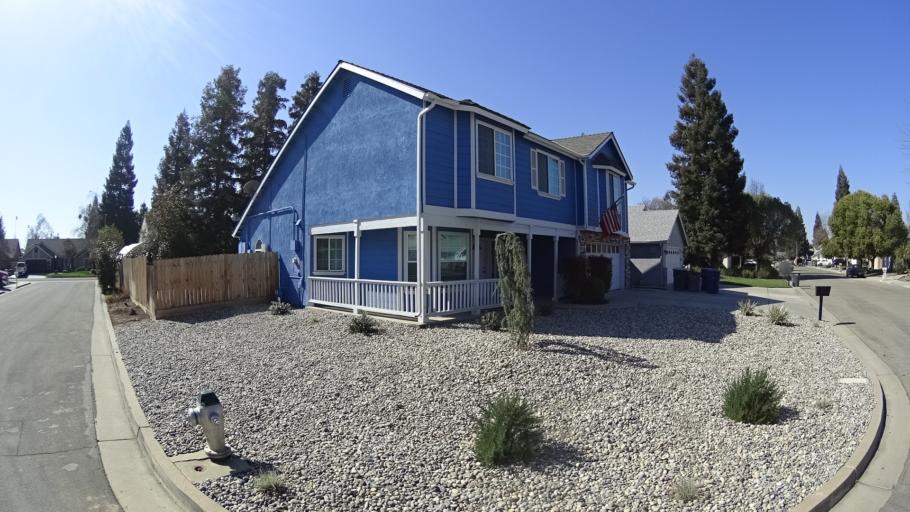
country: US
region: California
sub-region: Fresno County
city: Clovis
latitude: 36.8806
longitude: -119.7492
